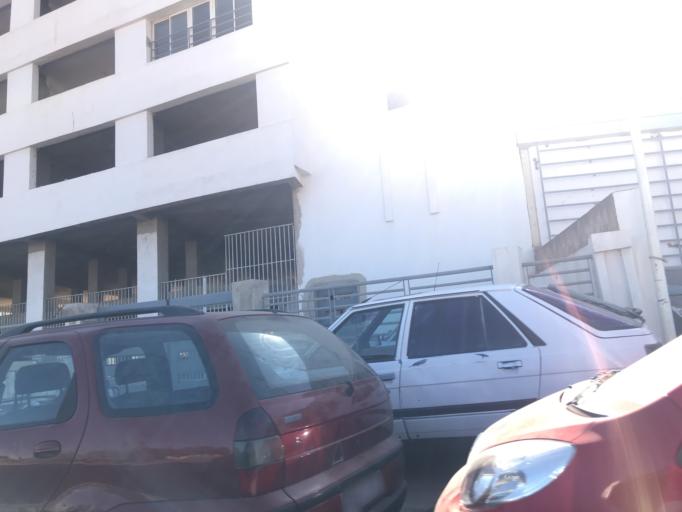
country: MA
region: Fes-Boulemane
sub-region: Fes
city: Fes
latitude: 33.9909
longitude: -5.0379
